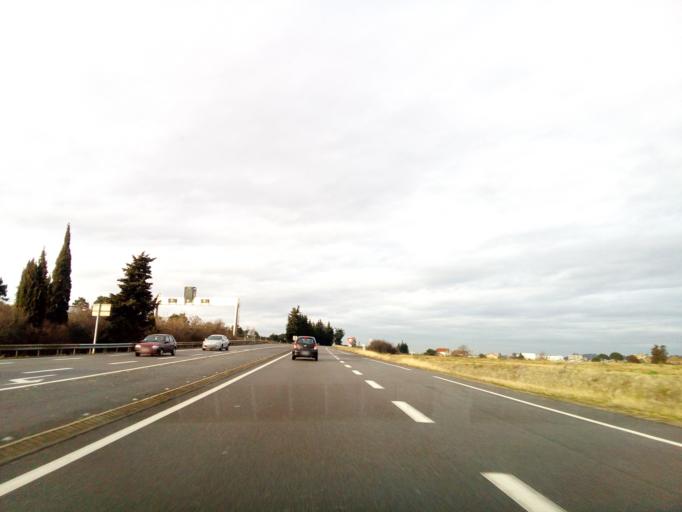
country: FR
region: Rhone-Alpes
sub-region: Departement de la Drome
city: Portes-les-Valence
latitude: 44.8795
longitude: 4.8669
